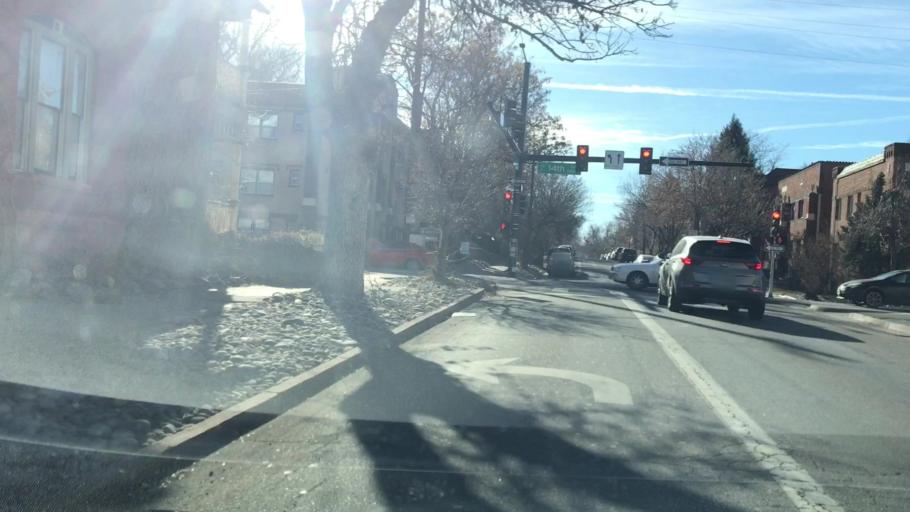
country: US
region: Colorado
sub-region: Denver County
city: Denver
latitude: 39.7388
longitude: -104.9741
